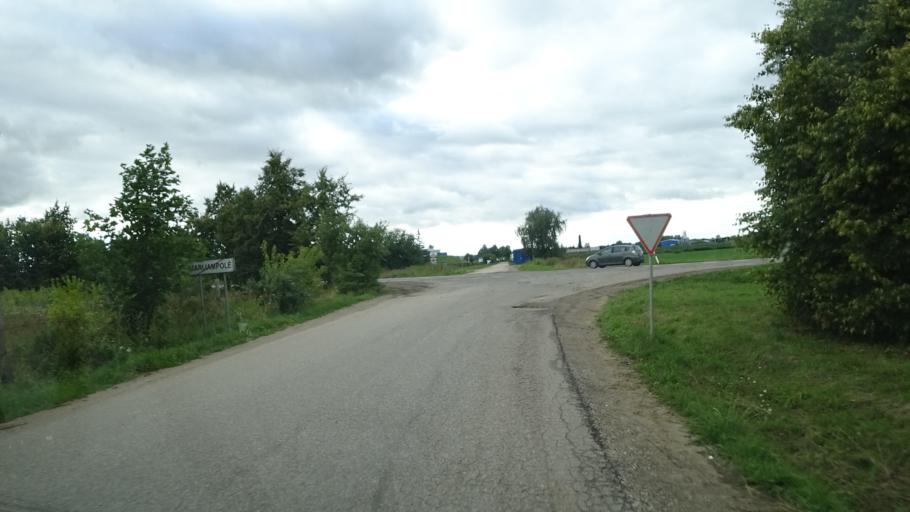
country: LT
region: Marijampoles apskritis
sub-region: Marijampole Municipality
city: Marijampole
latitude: 54.5831
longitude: 23.3622
